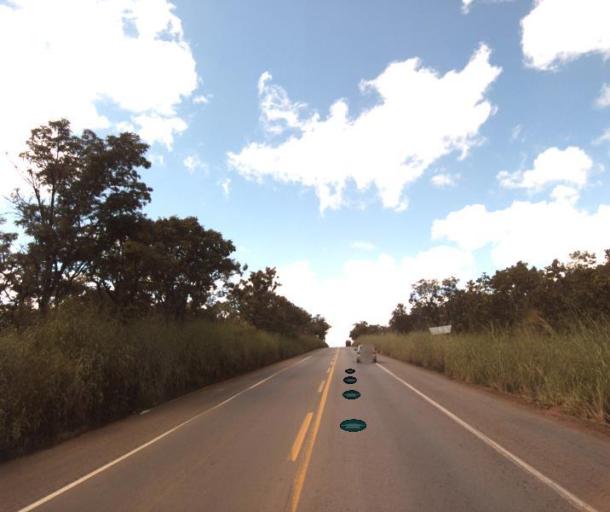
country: BR
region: Goias
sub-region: Jaragua
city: Jaragua
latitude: -15.8824
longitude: -49.2452
